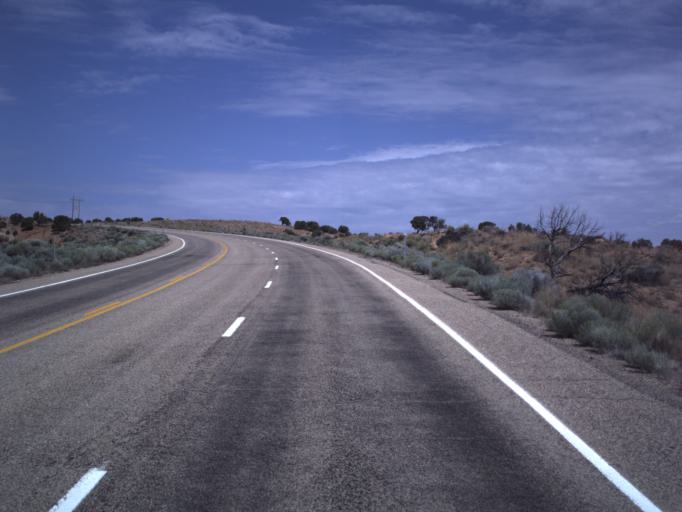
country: US
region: Utah
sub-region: Uintah County
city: Naples
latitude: 40.1401
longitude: -109.2728
